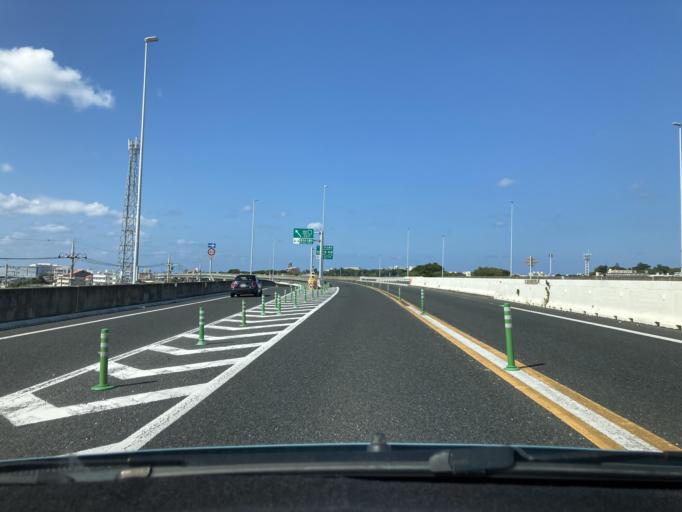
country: JP
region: Okinawa
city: Tomigusuku
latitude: 26.1756
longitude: 127.6726
